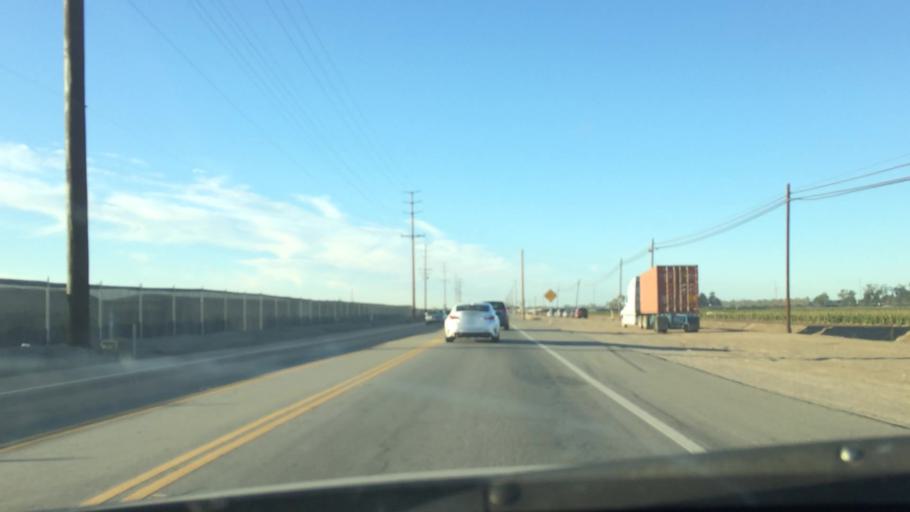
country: US
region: California
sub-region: Ventura County
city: El Rio
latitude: 34.2431
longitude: -119.1218
